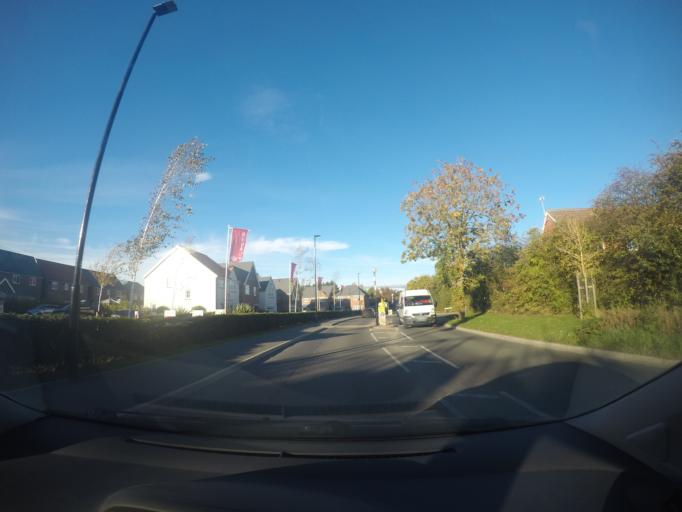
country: GB
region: England
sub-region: City of York
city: York
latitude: 53.9809
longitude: -1.0953
